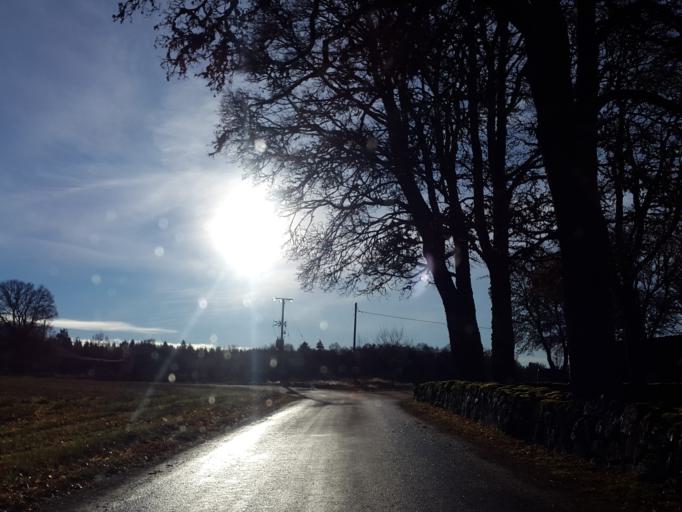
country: SE
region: Vaestra Goetaland
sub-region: Herrljunga Kommun
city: Herrljunga
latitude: 58.0630
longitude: 12.9526
